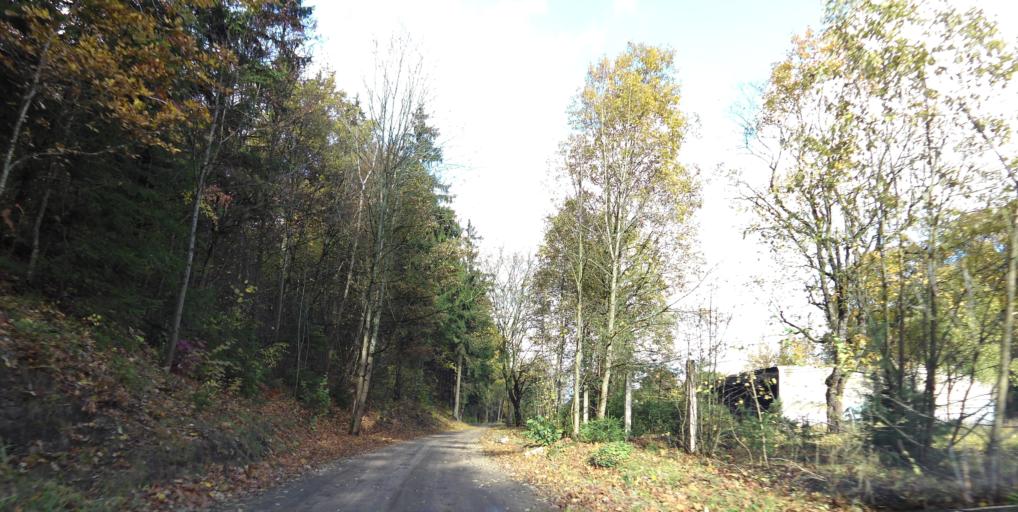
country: LT
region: Vilnius County
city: Vilkpede
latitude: 54.6556
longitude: 25.2577
